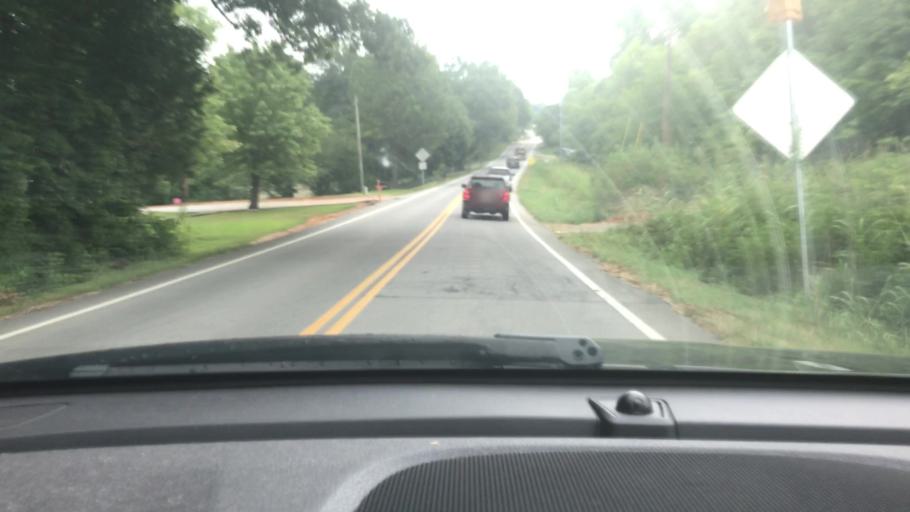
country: US
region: Tennessee
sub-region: Cheatham County
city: Ashland City
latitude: 36.2766
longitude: -87.1880
